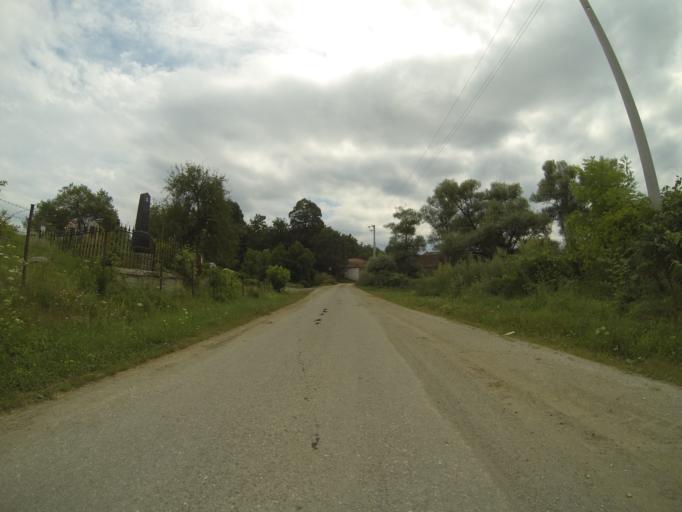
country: RO
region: Brasov
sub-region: Comuna Hoghiz
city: Hoghiz
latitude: 45.9861
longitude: 25.3843
